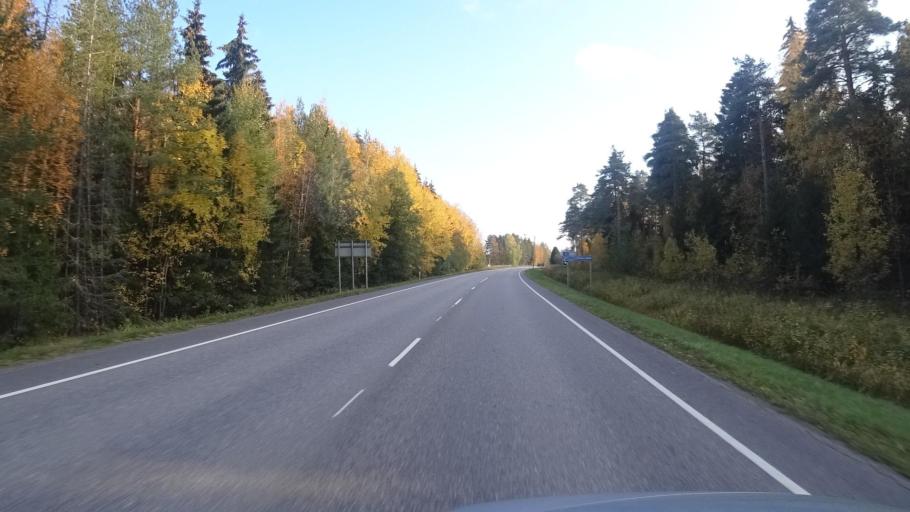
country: FI
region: Satakunta
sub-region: Rauma
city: Saekylae
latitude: 61.0659
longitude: 22.3220
